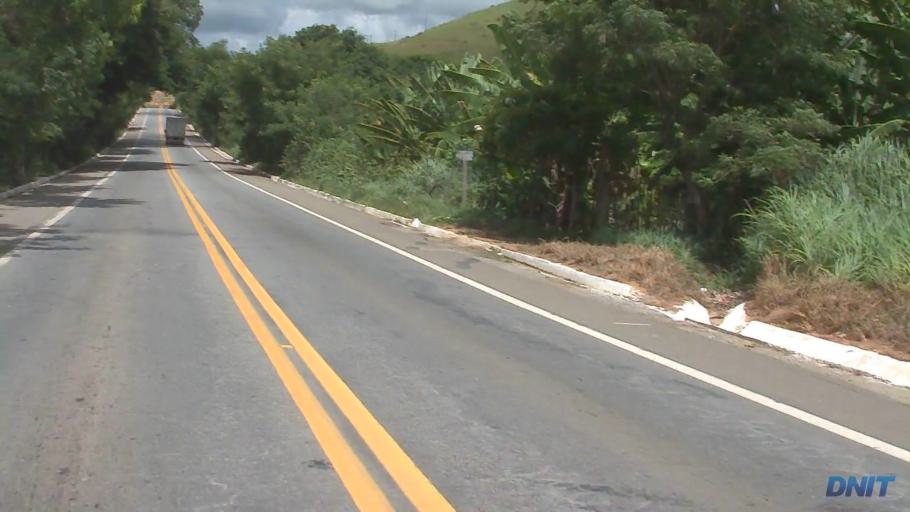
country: BR
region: Minas Gerais
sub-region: Governador Valadares
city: Governador Valadares
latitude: -18.9379
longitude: -42.0545
